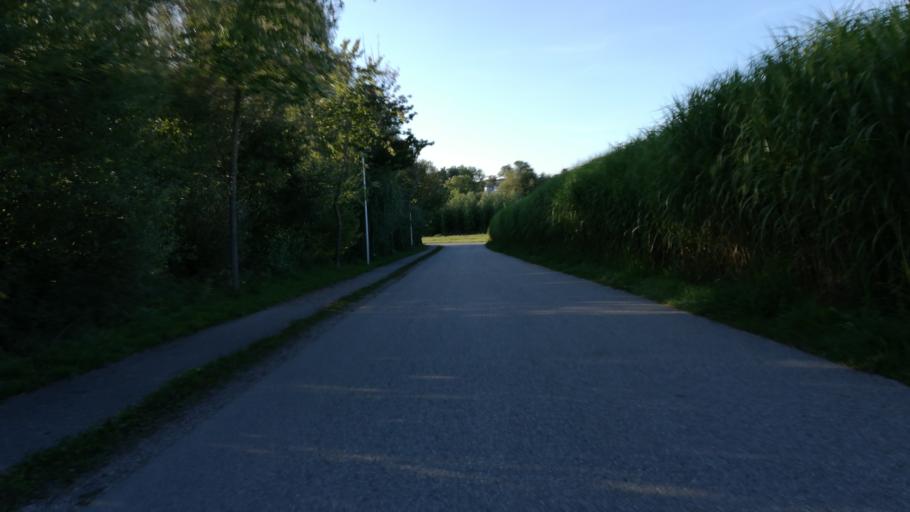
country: AT
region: Upper Austria
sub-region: Politischer Bezirk Grieskirchen
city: Bad Schallerbach
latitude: 48.1861
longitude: 13.9034
